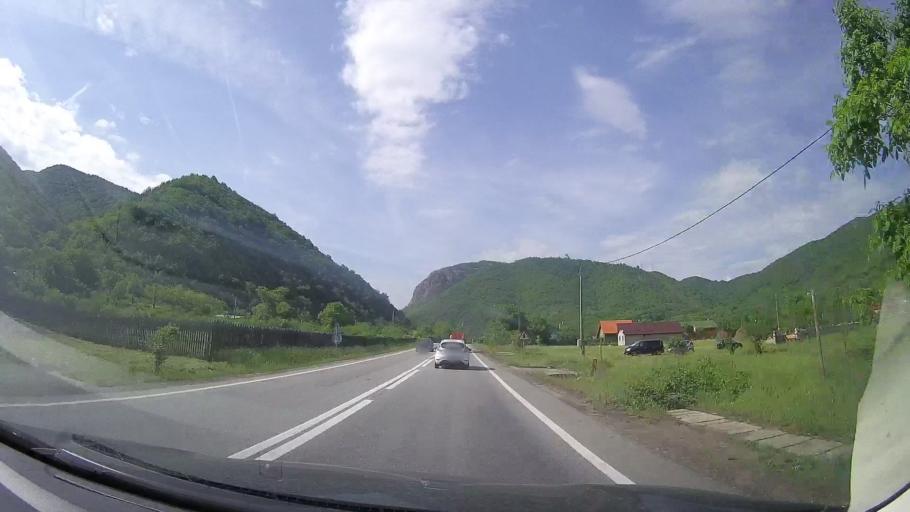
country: RO
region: Caras-Severin
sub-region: Comuna Mehadia
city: Mehadia
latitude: 44.8840
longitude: 22.3829
